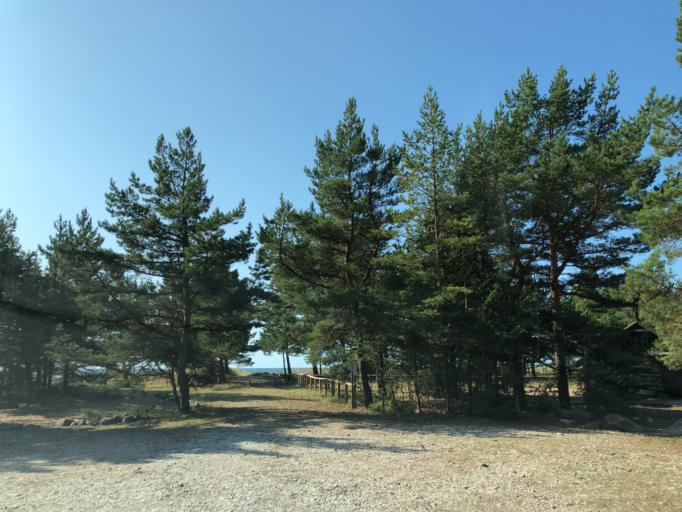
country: EE
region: Hiiumaa
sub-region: Kaerdla linn
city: Kardla
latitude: 58.9079
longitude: 22.1329
